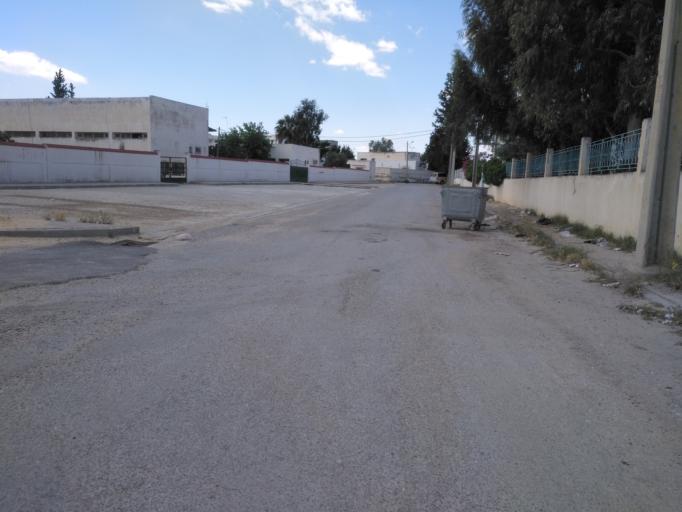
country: TN
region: Silyanah
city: Siliana
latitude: 36.0875
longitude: 9.3746
